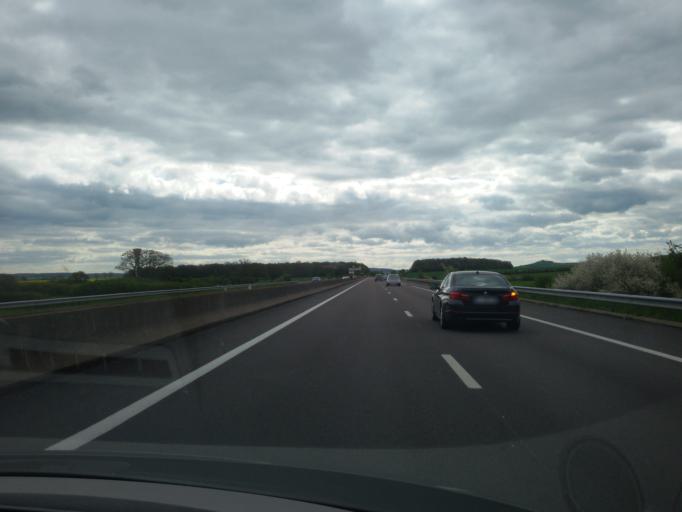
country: FR
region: Bourgogne
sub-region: Departement de la Cote-d'Or
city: Semur-en-Auxois
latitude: 47.3707
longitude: 4.4005
